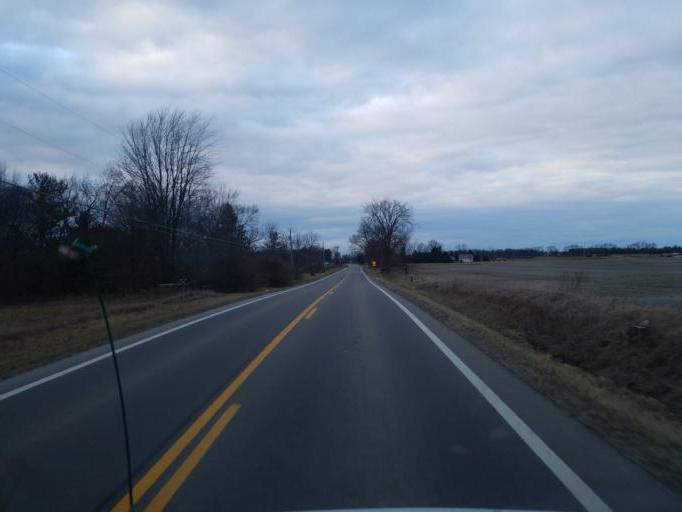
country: US
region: Ohio
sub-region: Delaware County
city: Delaware
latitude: 40.3340
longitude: -83.1318
